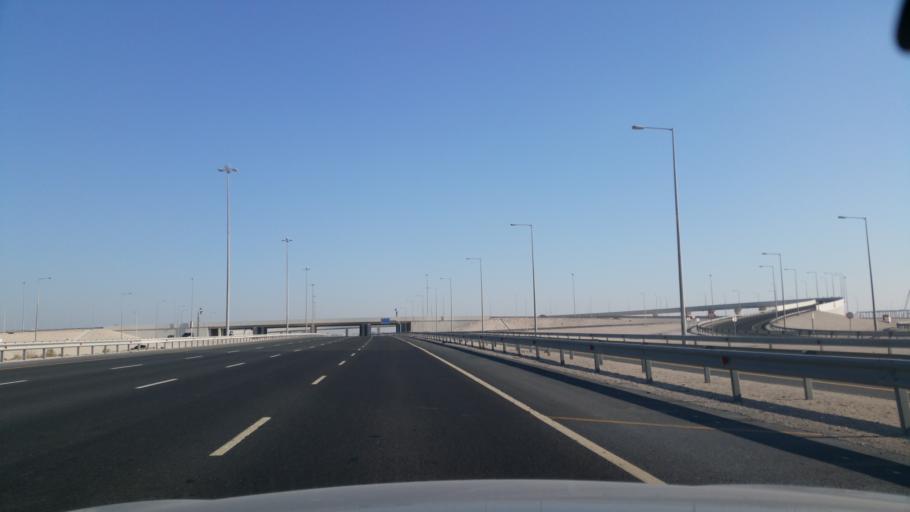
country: QA
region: Al Wakrah
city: Al Wukayr
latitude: 25.1259
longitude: 51.4839
